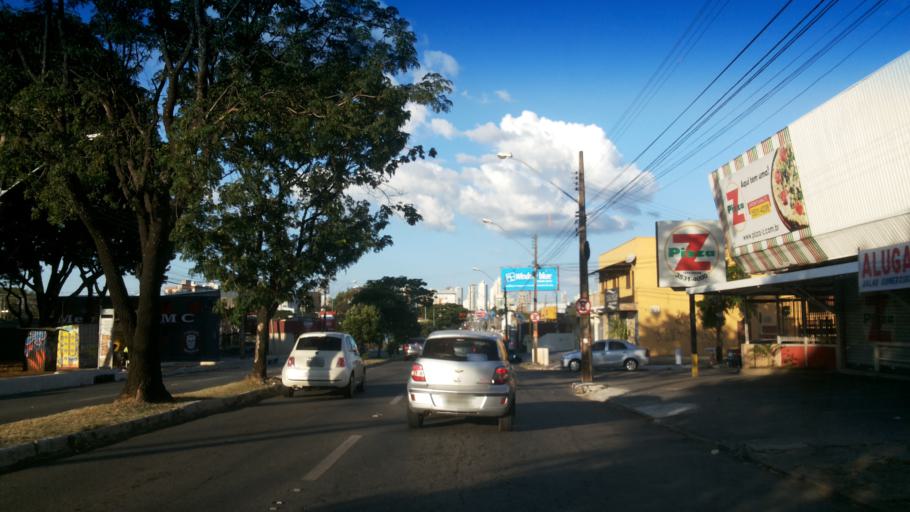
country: BR
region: Goias
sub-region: Goiania
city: Goiania
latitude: -16.7110
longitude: -49.2989
